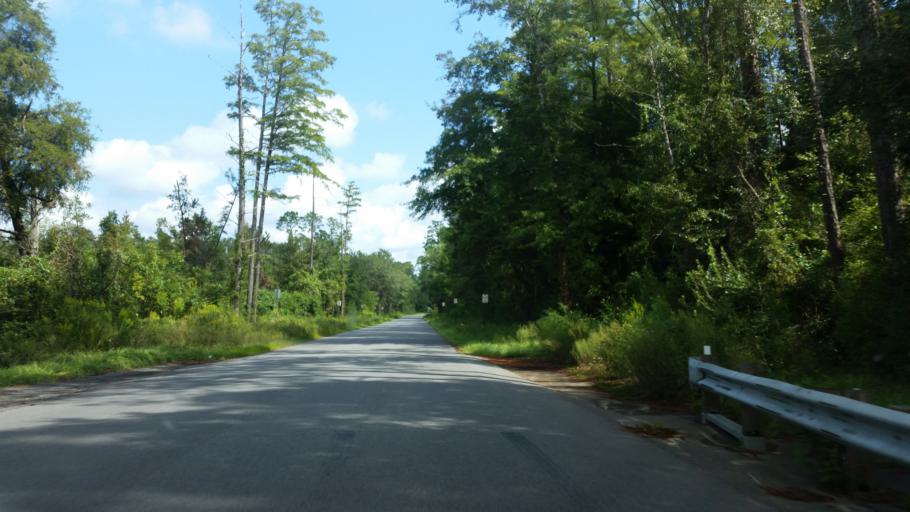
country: US
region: Florida
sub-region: Escambia County
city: Cantonment
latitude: 30.6914
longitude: -87.4396
